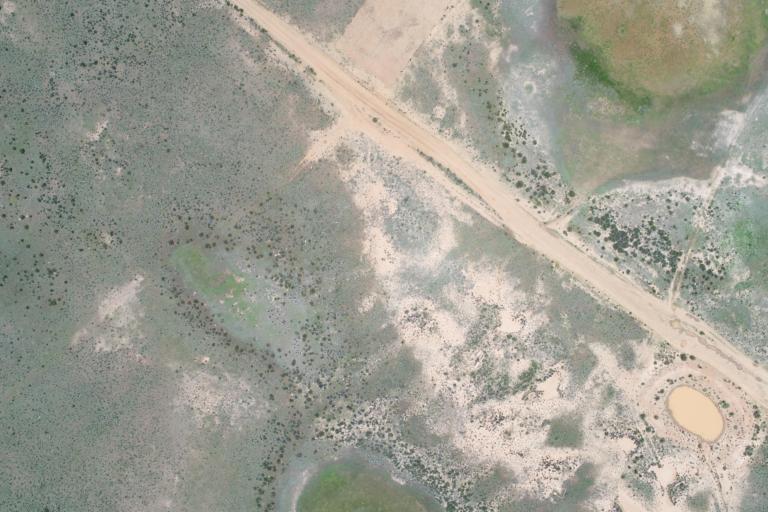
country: BO
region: La Paz
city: Curahuara de Carangas
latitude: -17.2872
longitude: -68.5145
